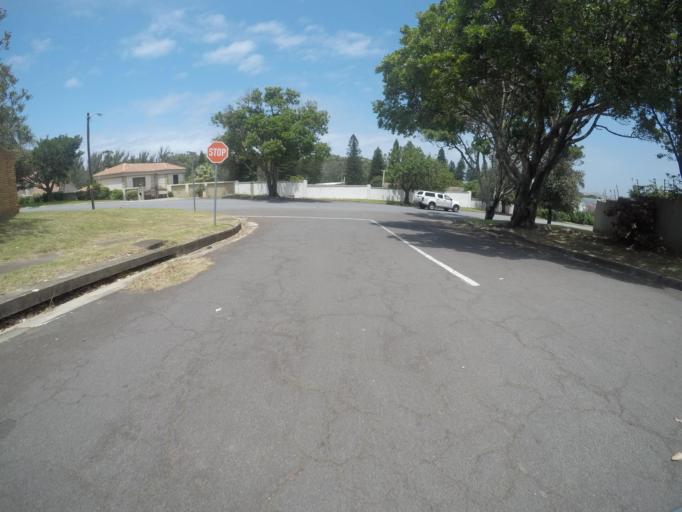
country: ZA
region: Eastern Cape
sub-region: Buffalo City Metropolitan Municipality
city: East London
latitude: -32.9994
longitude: 27.9285
